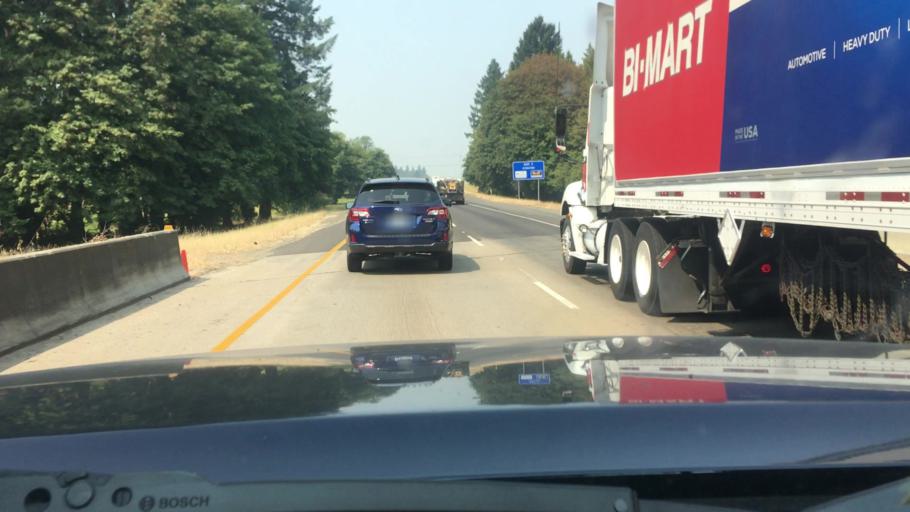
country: US
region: Oregon
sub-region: Clackamas County
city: Stafford
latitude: 45.3676
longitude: -122.6942
